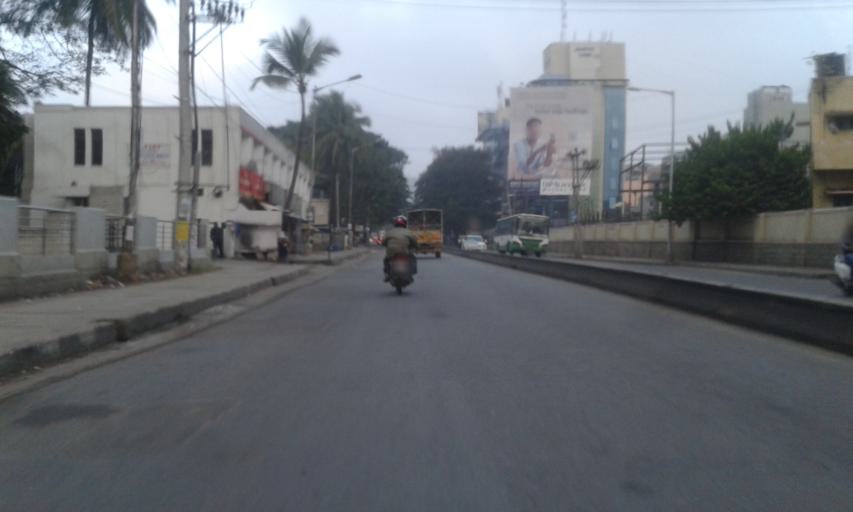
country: IN
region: Karnataka
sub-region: Bangalore Urban
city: Bangalore
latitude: 12.9320
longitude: 77.6133
